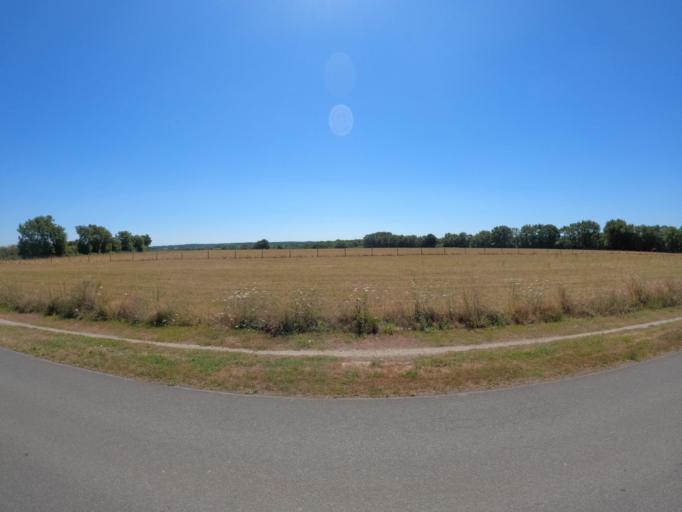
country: FR
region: Pays de la Loire
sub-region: Departement de la Loire-Atlantique
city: La Limouziniere
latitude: 46.9582
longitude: -1.5971
